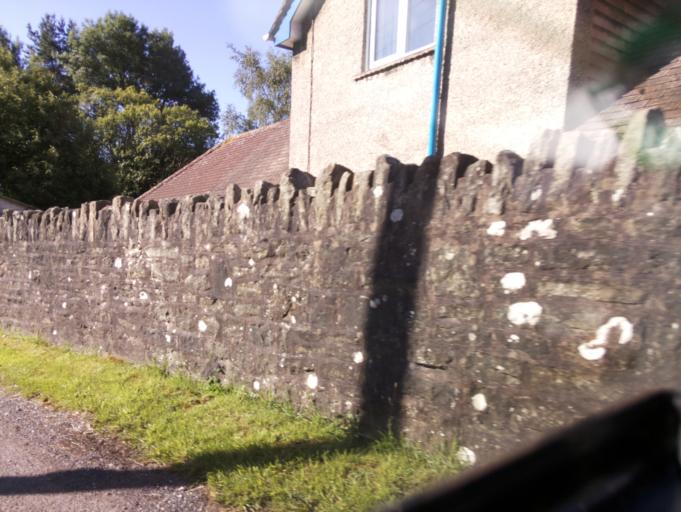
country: GB
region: England
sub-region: Gloucestershire
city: Coleford
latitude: 51.7979
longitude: -2.6071
